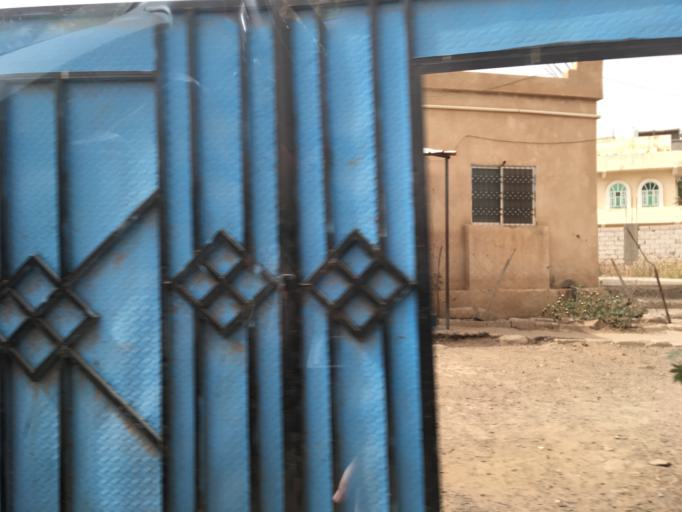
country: YE
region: Ad Dali'
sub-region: Ad Dhale'e
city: Dhalie
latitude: 13.7081
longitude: 44.7367
